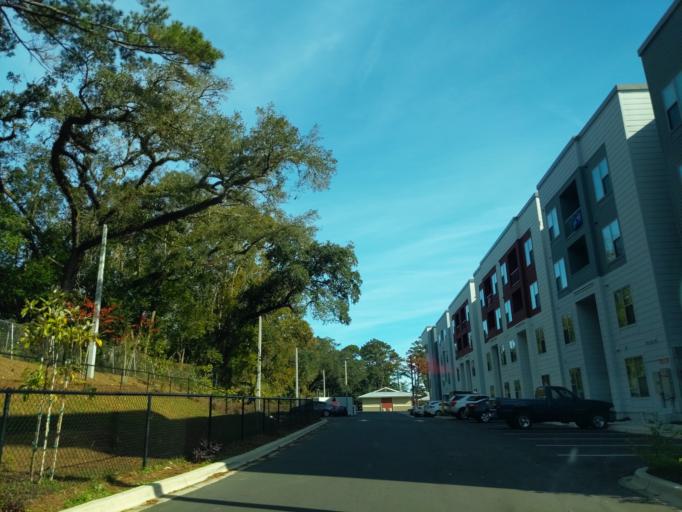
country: US
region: Florida
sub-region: Leon County
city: Tallahassee
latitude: 30.4415
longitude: -84.3122
